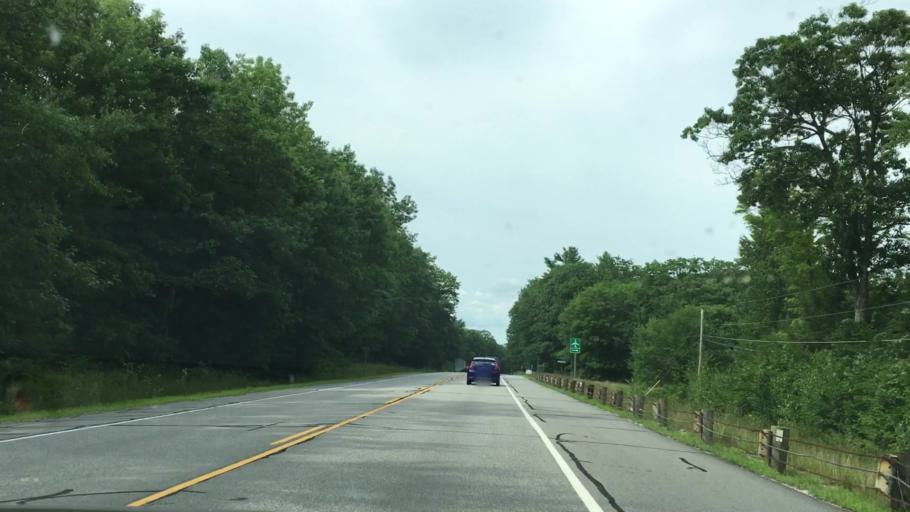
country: US
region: New Hampshire
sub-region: Hillsborough County
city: Antrim
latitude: 43.0701
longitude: -71.9162
